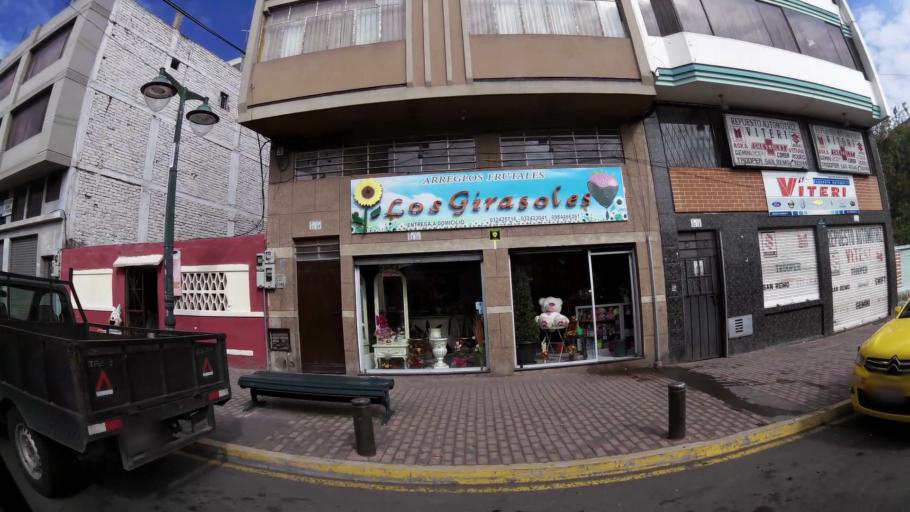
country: EC
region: Tungurahua
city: Ambato
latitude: -1.2305
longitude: -78.6286
